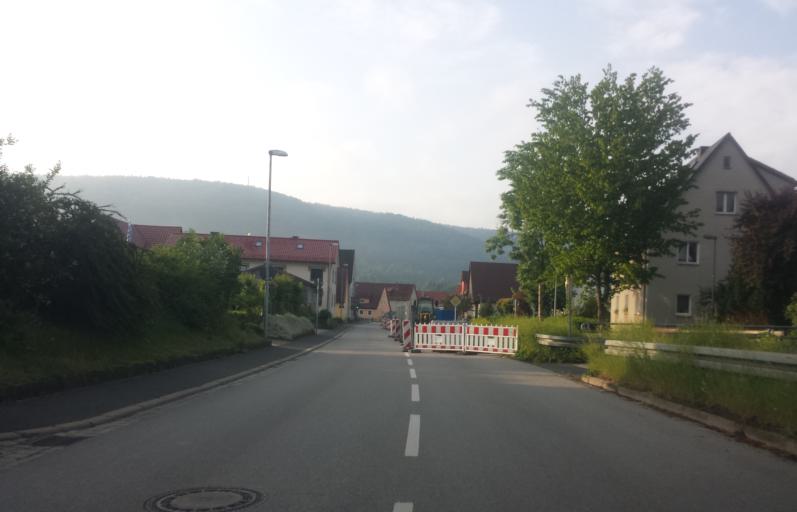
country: DE
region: Bavaria
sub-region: Upper Franconia
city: Ebermannstadt
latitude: 49.7843
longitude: 11.1821
